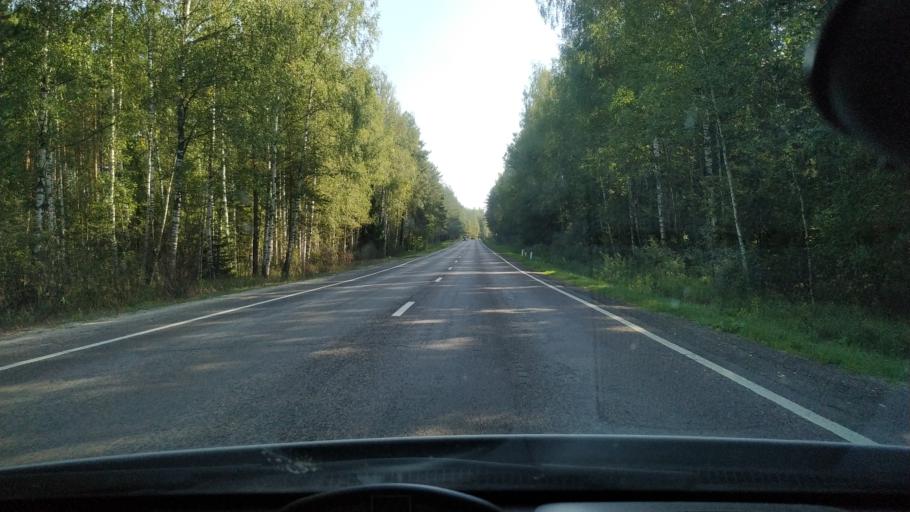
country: RU
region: Moskovskaya
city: Dmitrovskiy Pogost
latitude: 55.2341
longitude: 39.9555
